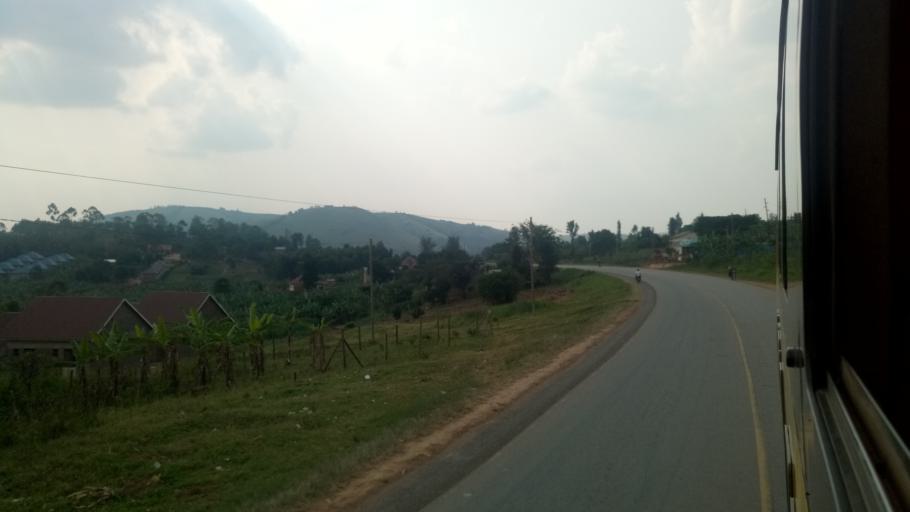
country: UG
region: Western Region
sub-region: Mbarara District
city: Mbarara
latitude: -0.5493
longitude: 30.7144
